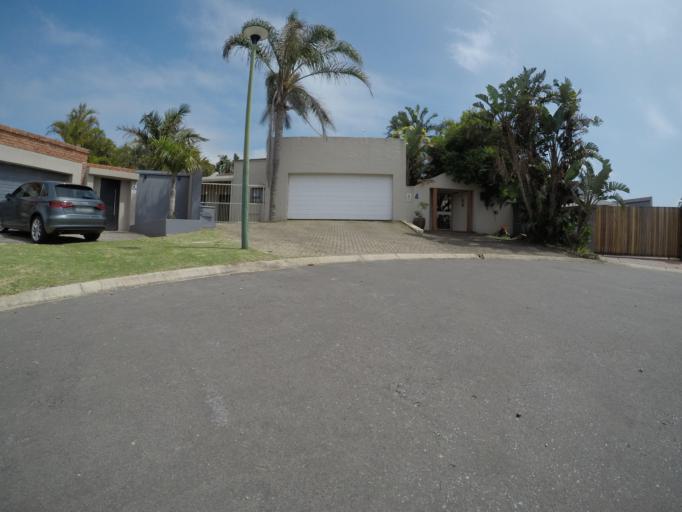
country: ZA
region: Eastern Cape
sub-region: Buffalo City Metropolitan Municipality
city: East London
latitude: -32.9363
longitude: 28.0277
